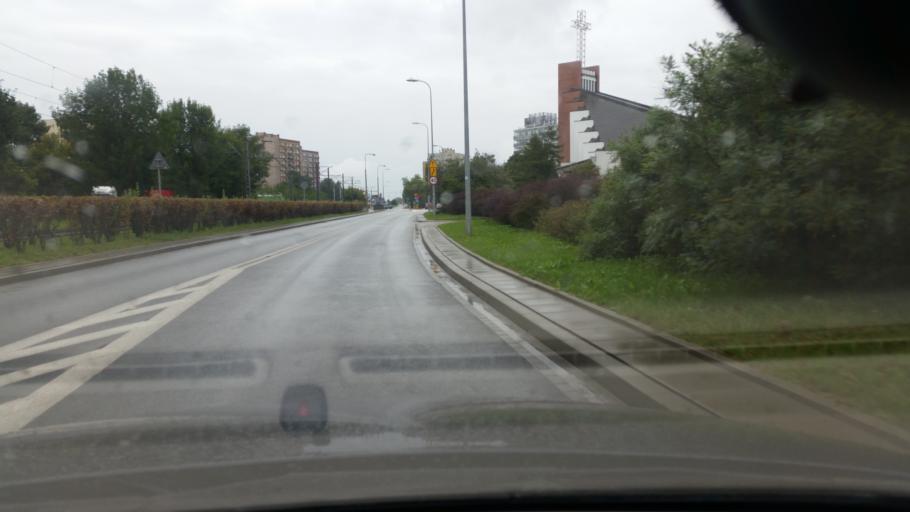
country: PL
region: Masovian Voivodeship
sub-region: Warszawa
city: Targowek
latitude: 52.2918
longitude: 21.0290
